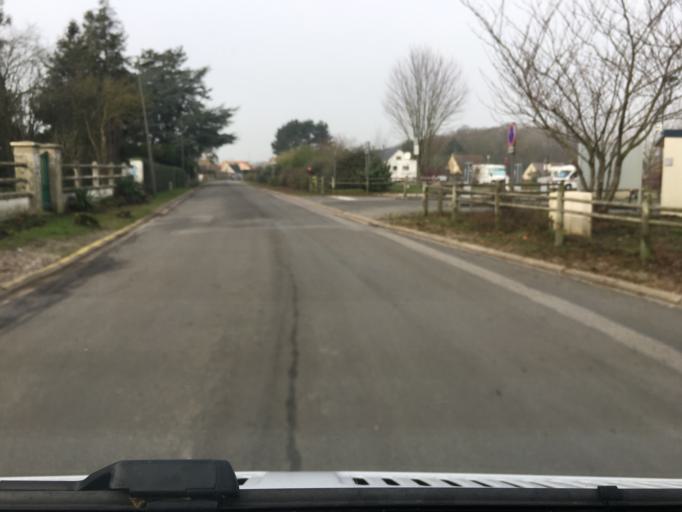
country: FR
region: Picardie
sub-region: Departement de la Somme
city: Saint-Valery-sur-Somme
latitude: 50.1821
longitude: 1.6293
